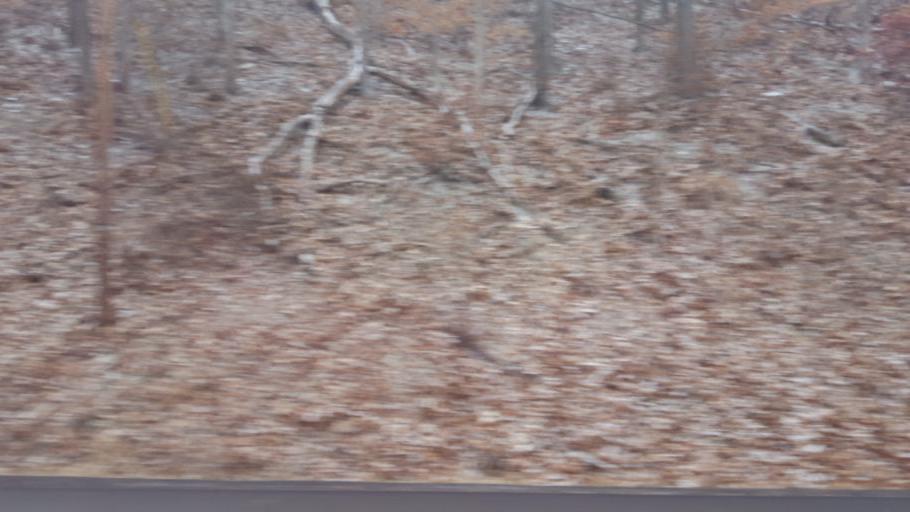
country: US
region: Ohio
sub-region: Coshocton County
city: Coshocton
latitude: 40.3389
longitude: -82.0134
